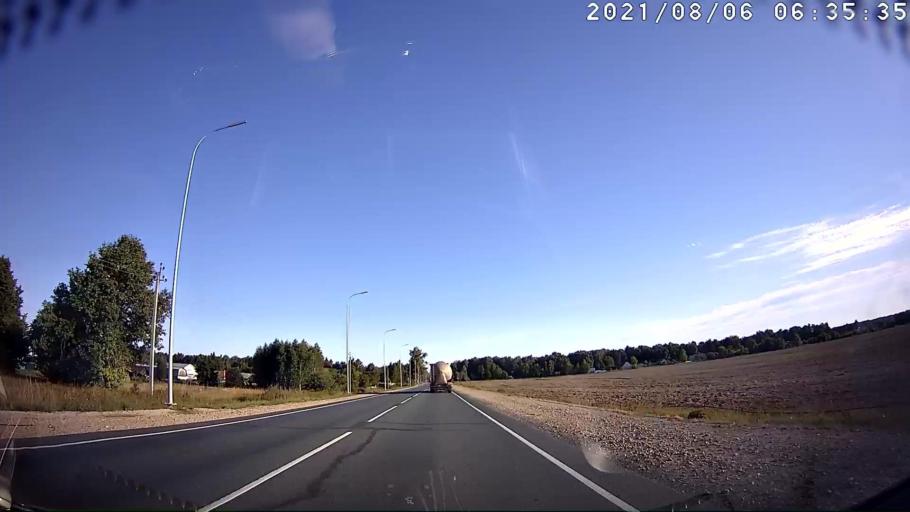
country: RU
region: Mariy-El
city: Suslonger
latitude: 56.2204
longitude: 48.2358
